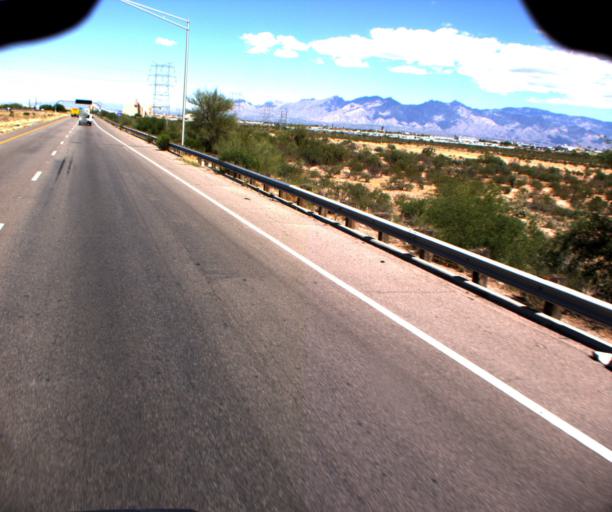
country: US
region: Arizona
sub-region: Pima County
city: Tucson
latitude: 32.1406
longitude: -110.8907
